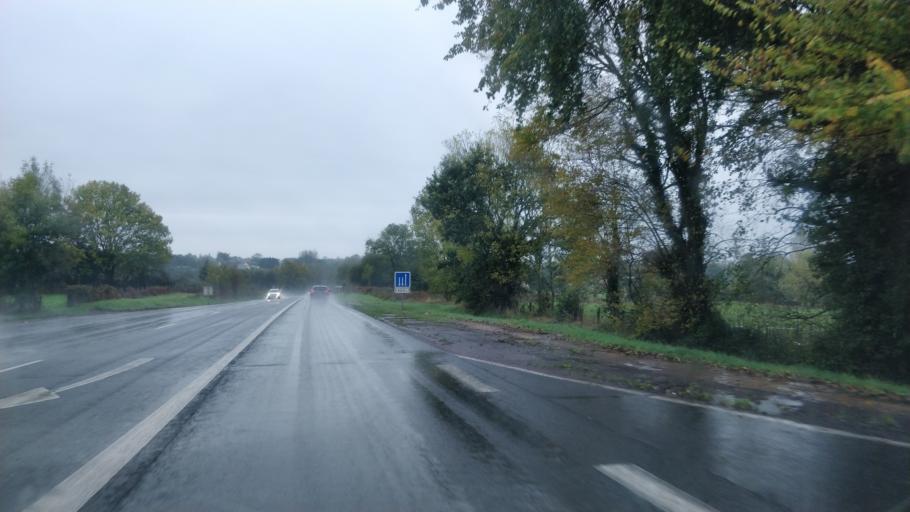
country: FR
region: Lower Normandy
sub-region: Departement de la Manche
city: Saint-Planchers
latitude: 48.8270
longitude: -1.5447
